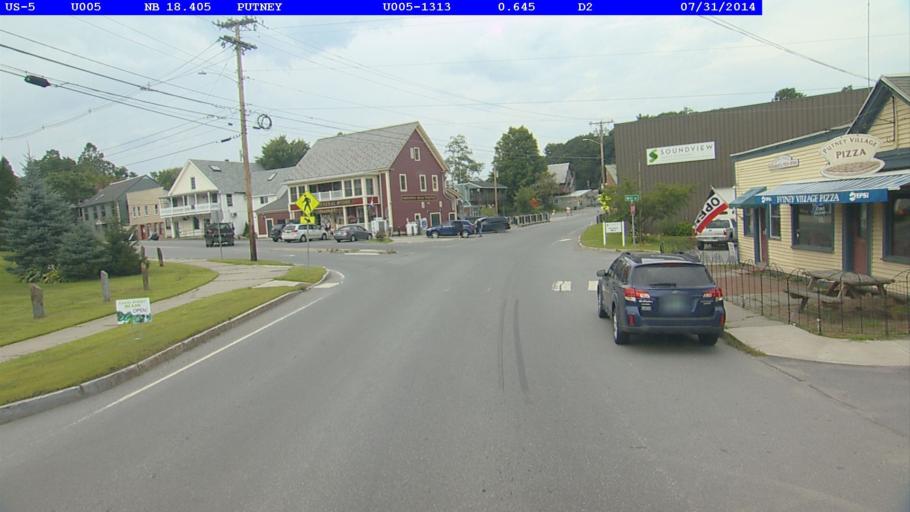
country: US
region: New Hampshire
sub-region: Cheshire County
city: Westmoreland
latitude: 42.9748
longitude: -72.5217
